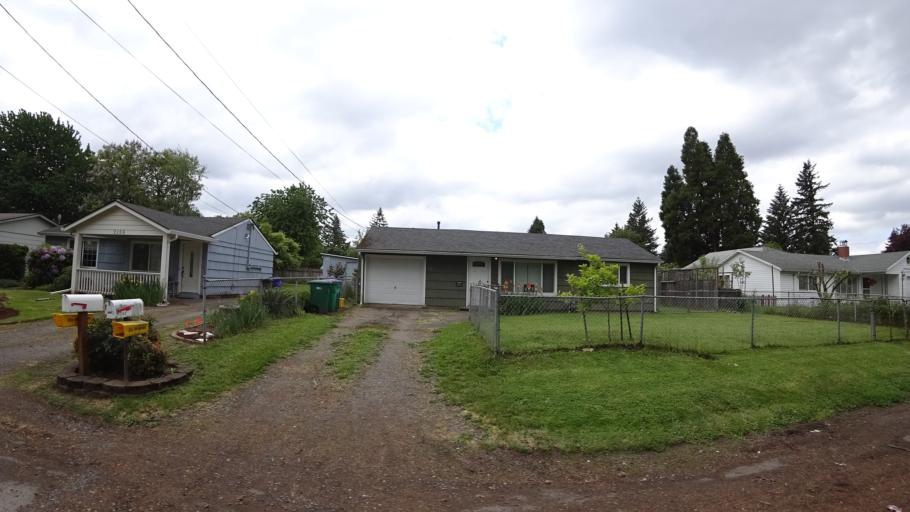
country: US
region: Oregon
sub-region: Multnomah County
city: Lents
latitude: 45.5072
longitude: -122.5408
